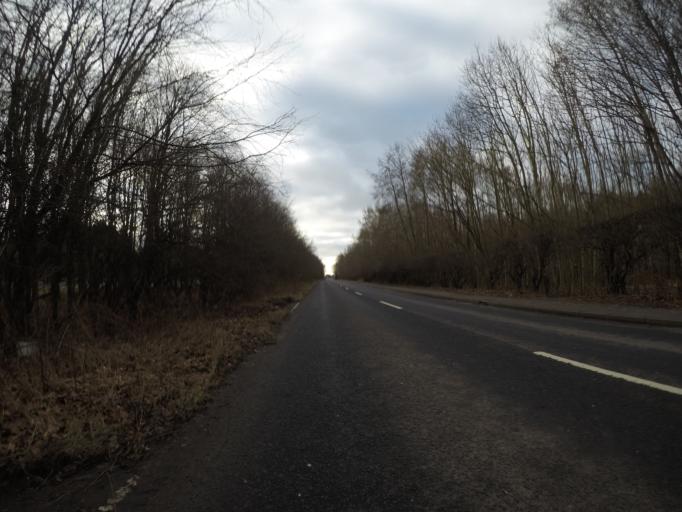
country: GB
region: Scotland
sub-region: North Ayrshire
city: Dreghorn
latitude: 55.5802
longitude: -4.6439
